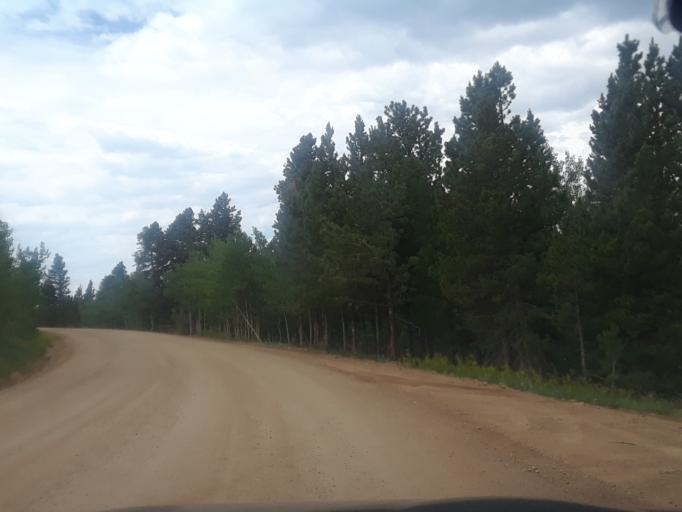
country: US
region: Colorado
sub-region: Boulder County
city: Nederland
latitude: 40.0452
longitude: -105.5167
